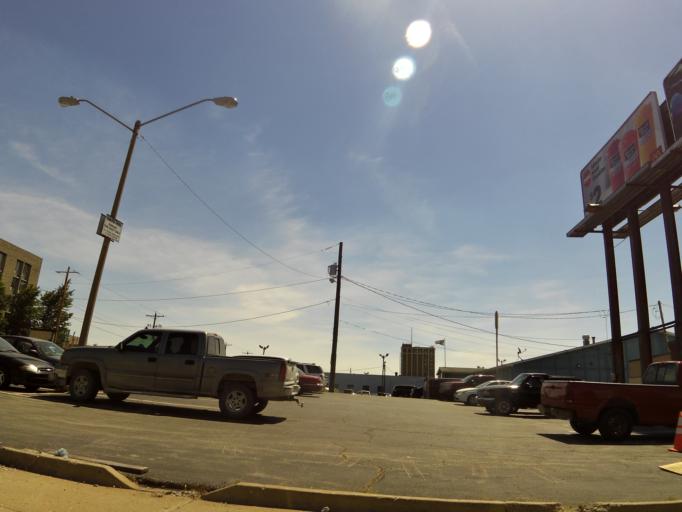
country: US
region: Illinois
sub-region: Vermilion County
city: Danville
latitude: 40.1250
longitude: -87.6355
